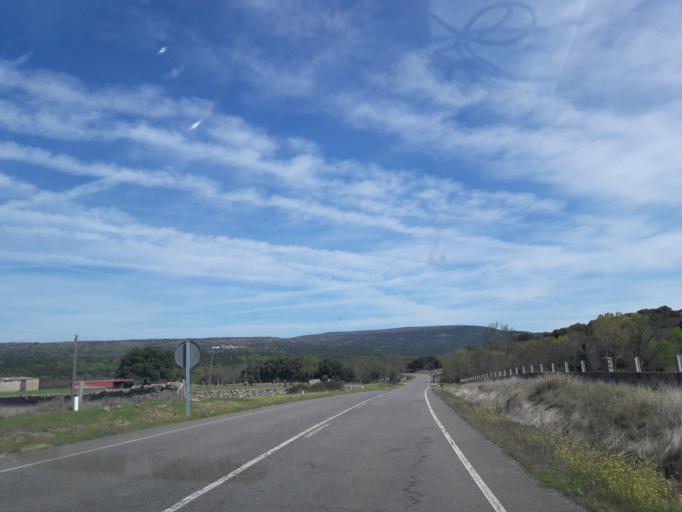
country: ES
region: Castille and Leon
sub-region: Provincia de Salamanca
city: Ledrada
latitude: 40.4767
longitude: -5.7273
